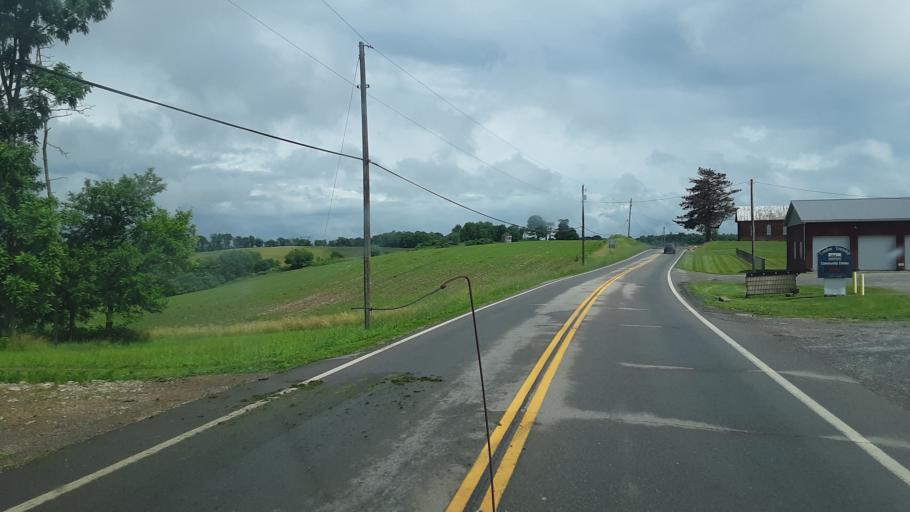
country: US
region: Ohio
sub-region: Carroll County
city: Carrollton
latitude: 40.4621
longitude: -81.0007
